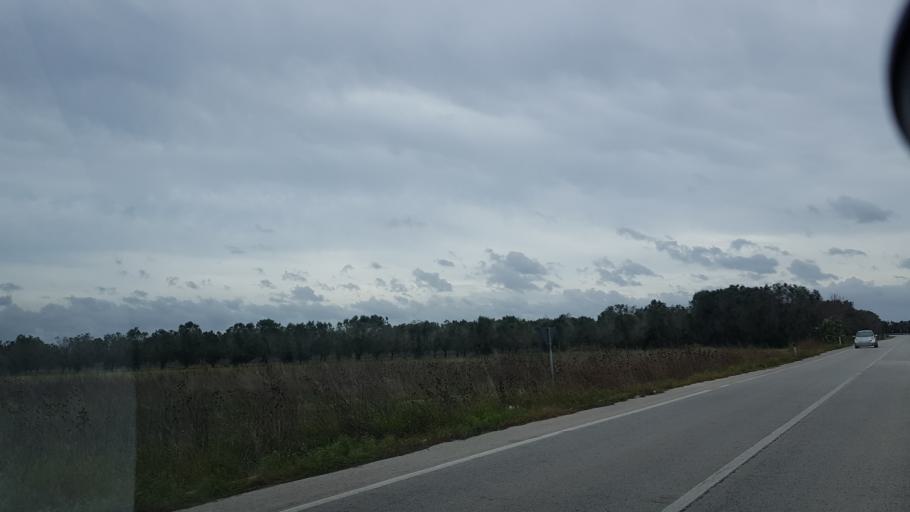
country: IT
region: Apulia
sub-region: Provincia di Lecce
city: Guagnano
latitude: 40.3995
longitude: 17.9183
